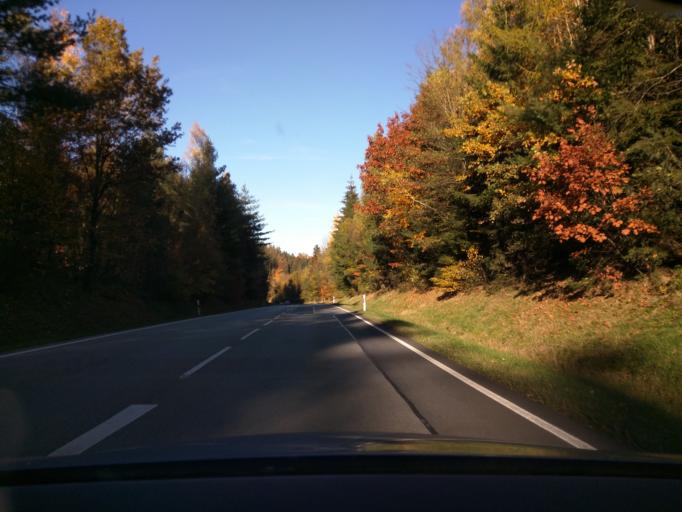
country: DE
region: Bavaria
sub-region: Lower Bavaria
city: Salzweg
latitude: 48.6015
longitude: 13.4777
